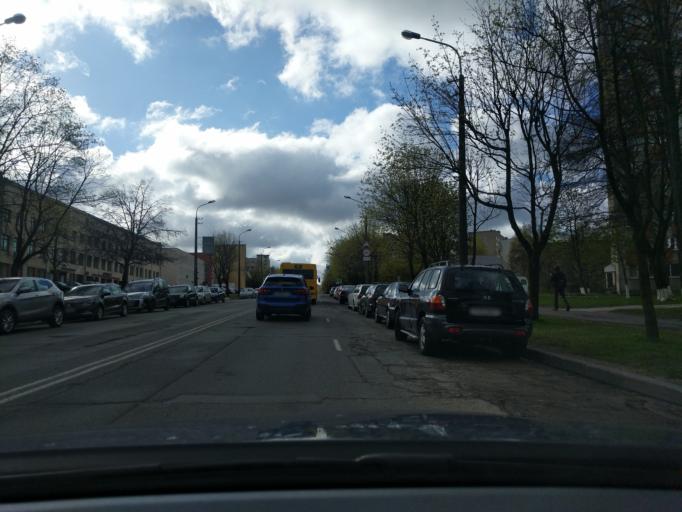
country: BY
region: Minsk
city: Novoye Medvezhino
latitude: 53.9163
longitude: 27.5032
